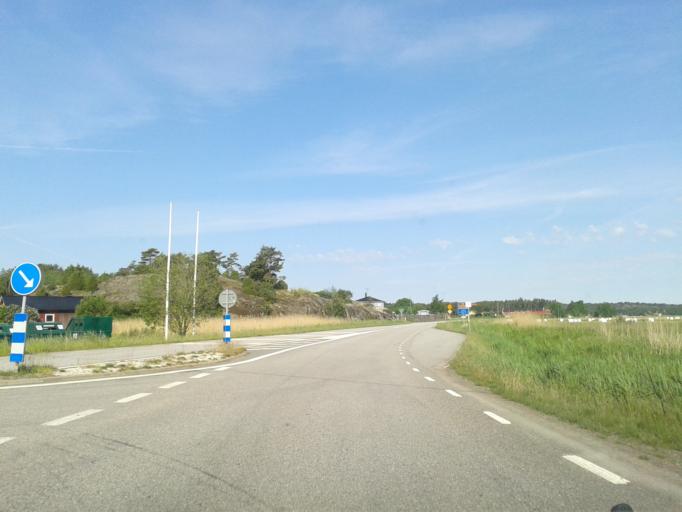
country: SE
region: Vaestra Goetaland
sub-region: Stromstads Kommun
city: Stroemstad
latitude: 58.8599
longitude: 11.2547
